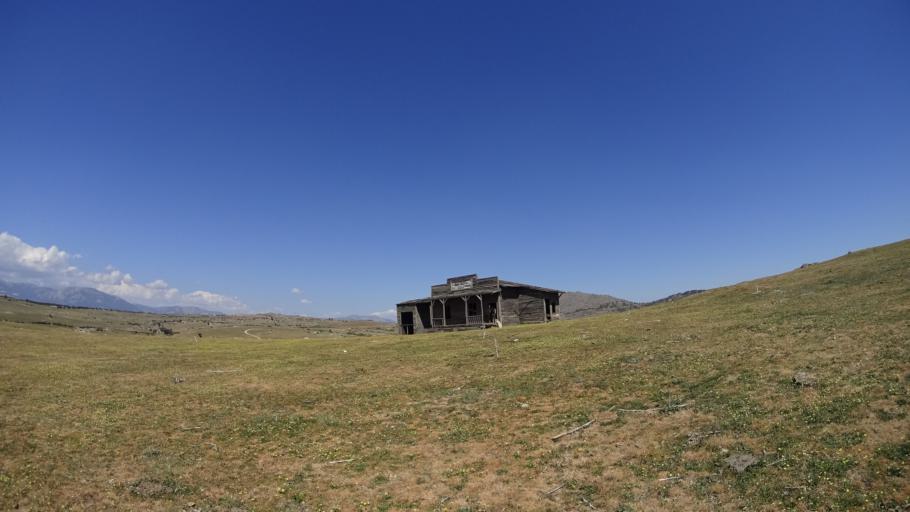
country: ES
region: Madrid
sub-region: Provincia de Madrid
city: Colmenar Viejo
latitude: 40.6905
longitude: -3.7508
